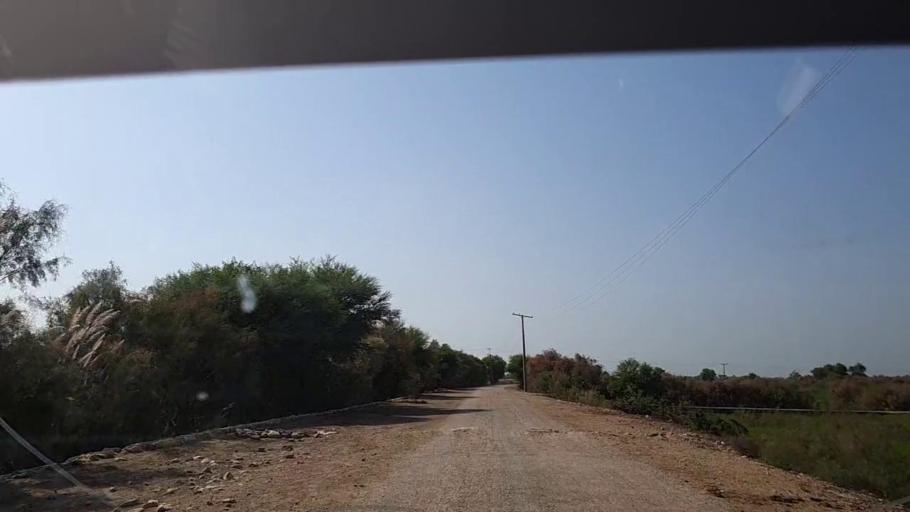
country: PK
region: Sindh
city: Ghauspur
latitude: 28.1970
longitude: 69.0460
